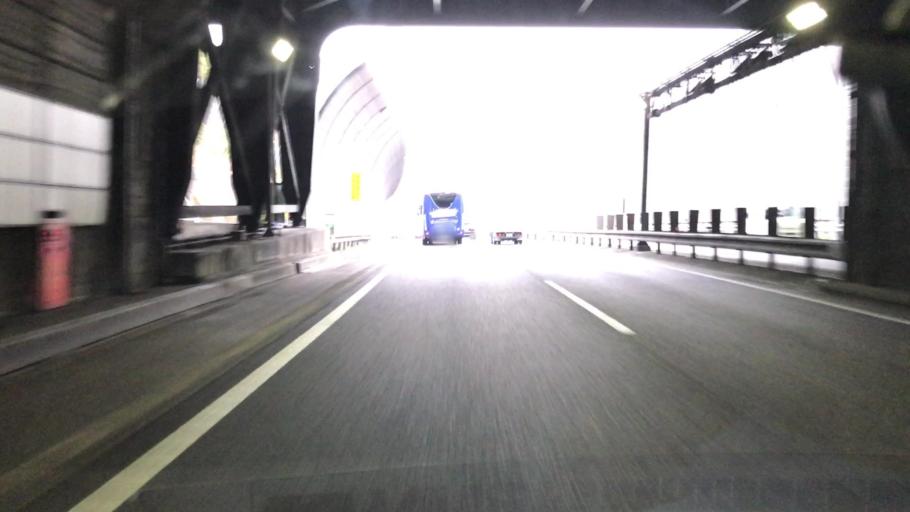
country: JP
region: Hyogo
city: Akashi
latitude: 34.6580
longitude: 135.0325
